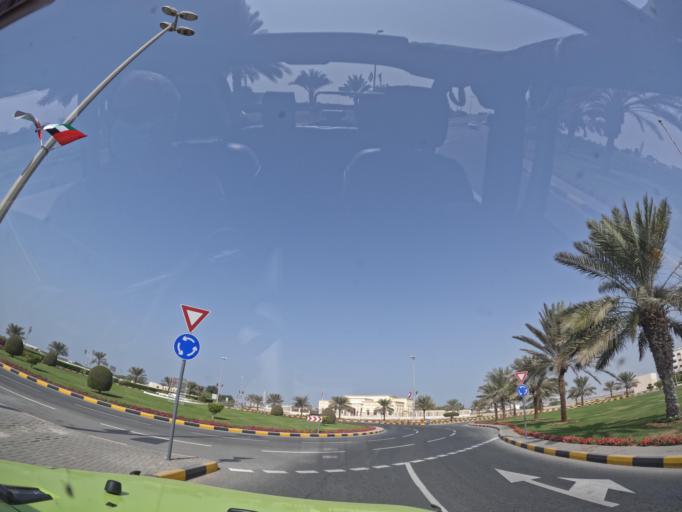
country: AE
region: Umm al Qaywayn
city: Umm al Qaywayn
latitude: 25.4791
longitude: 55.5226
